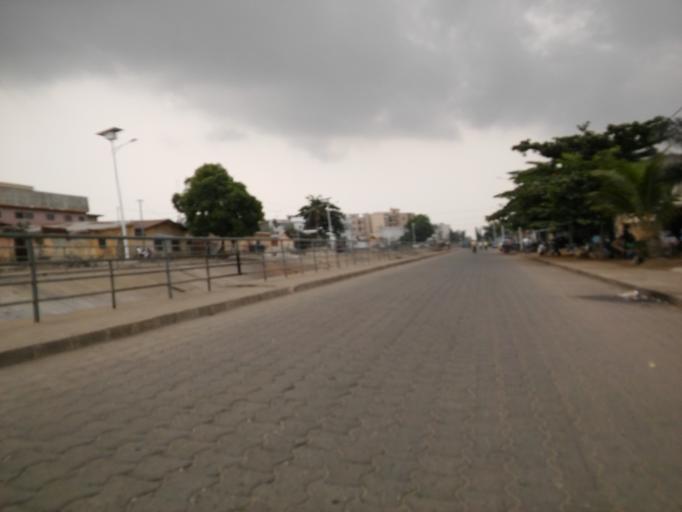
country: BJ
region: Littoral
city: Cotonou
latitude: 6.3818
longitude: 2.4227
